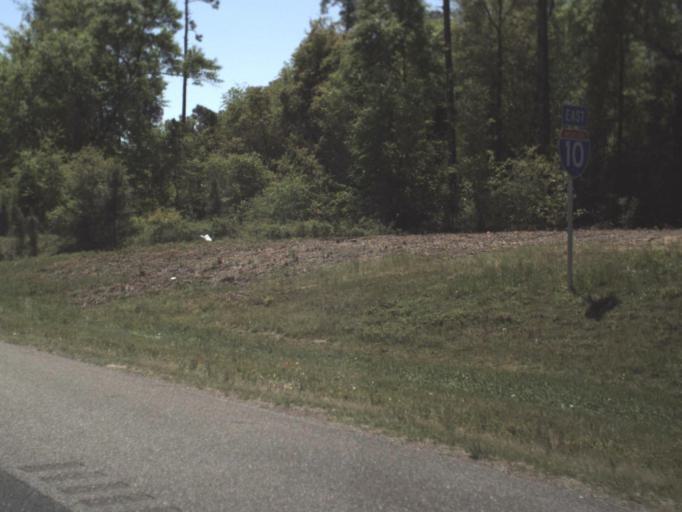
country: US
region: Florida
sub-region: Escambia County
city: Ensley
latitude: 30.5177
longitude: -87.3070
